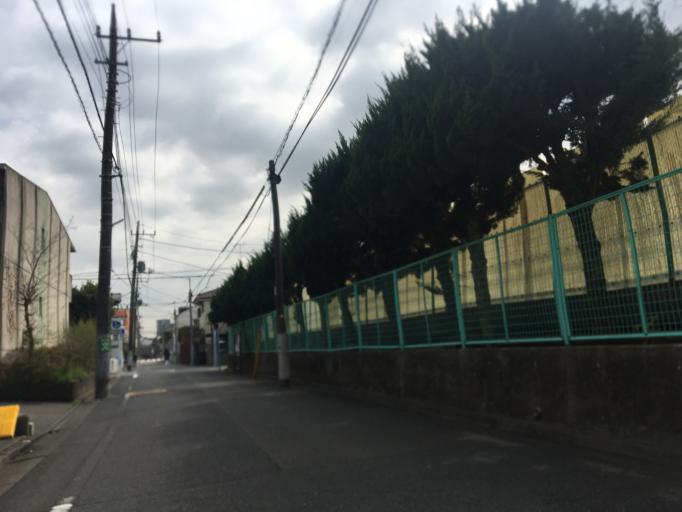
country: JP
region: Tokyo
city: Musashino
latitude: 35.7111
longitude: 139.5970
